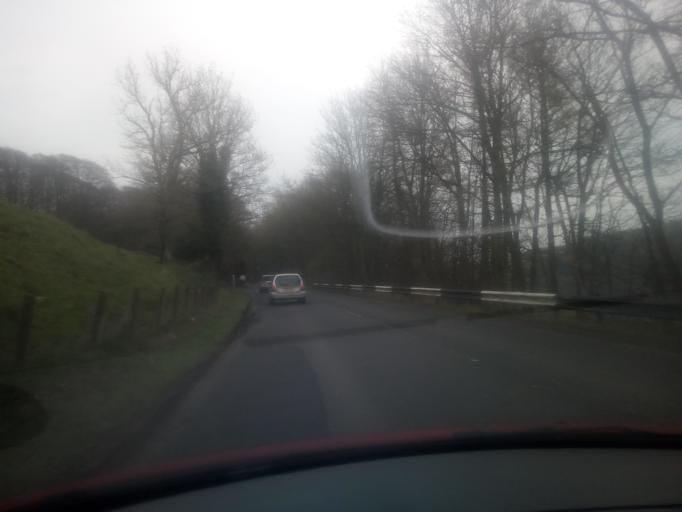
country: GB
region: Scotland
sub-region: The Scottish Borders
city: Galashiels
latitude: 55.6452
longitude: -2.8547
